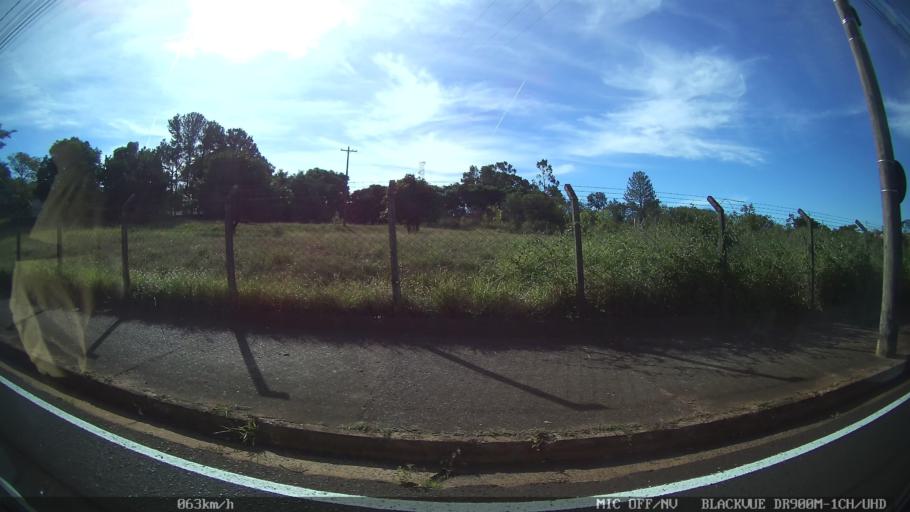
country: BR
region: Sao Paulo
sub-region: Sao Jose Do Rio Preto
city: Sao Jose do Rio Preto
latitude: -20.8017
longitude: -49.3520
